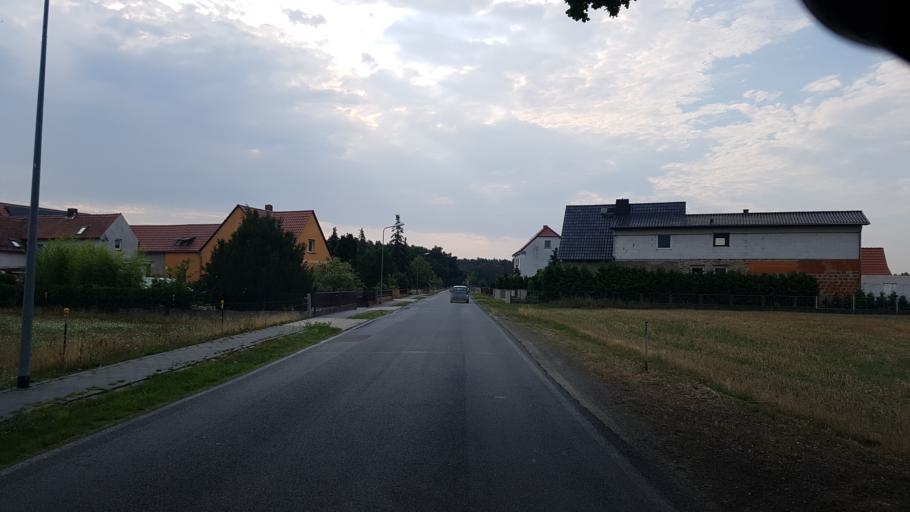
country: DE
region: Brandenburg
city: Lindenau
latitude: 51.3980
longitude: 13.7310
